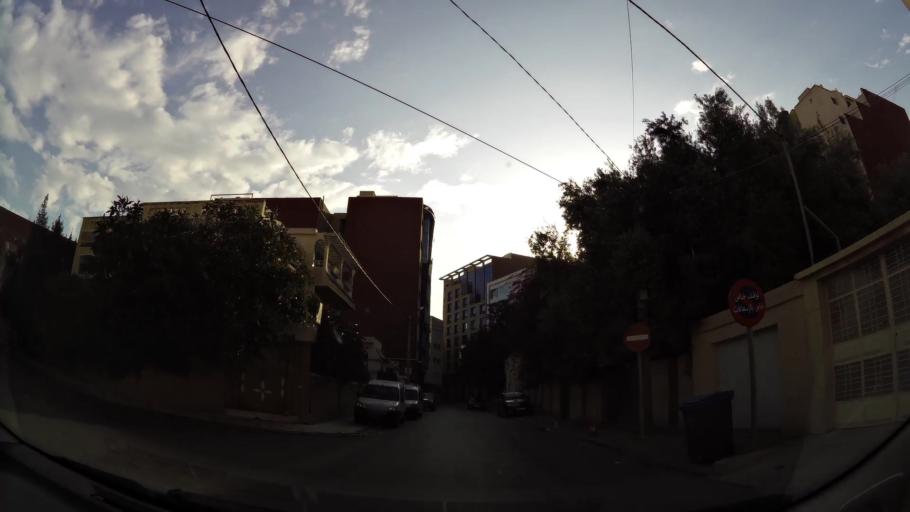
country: MA
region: Oriental
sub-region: Oujda-Angad
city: Oujda
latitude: 34.6790
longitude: -1.9203
